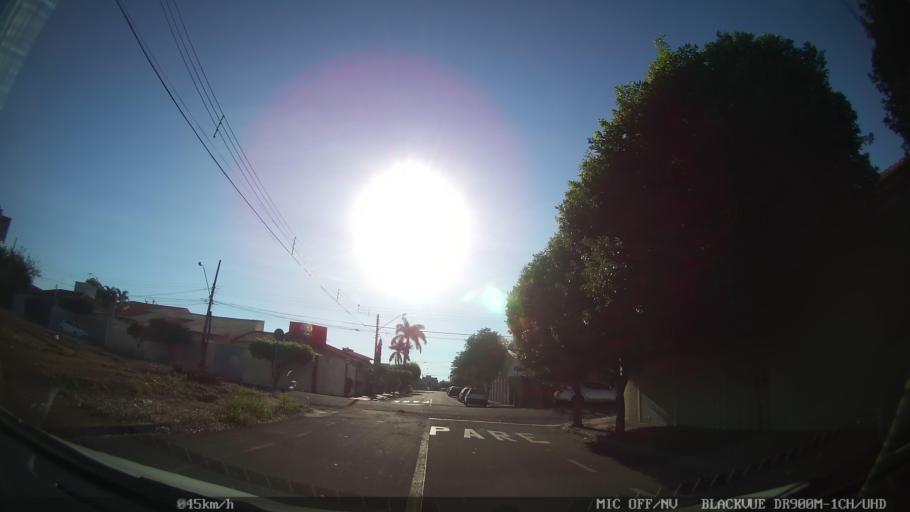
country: BR
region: Sao Paulo
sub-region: Sao Jose Do Rio Preto
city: Sao Jose do Rio Preto
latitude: -20.8237
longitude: -49.4076
